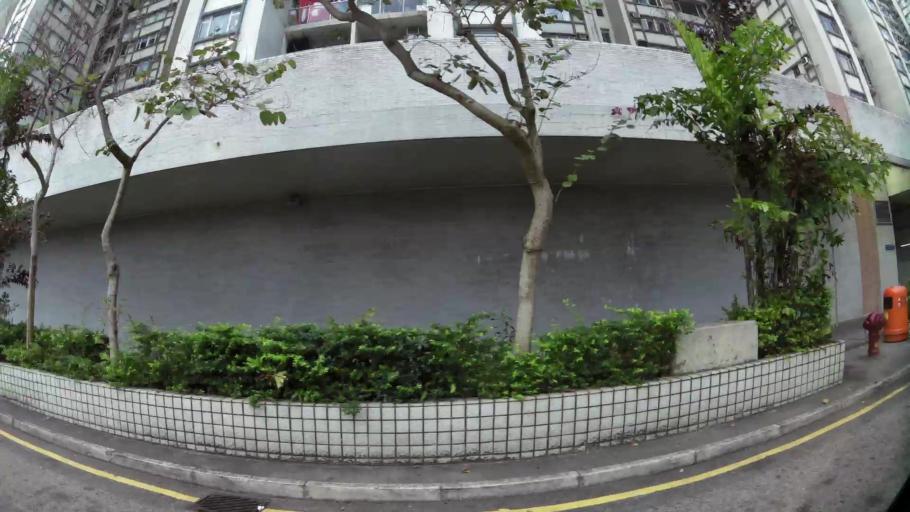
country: HK
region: Kowloon City
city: Kowloon
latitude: 22.2863
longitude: 114.2238
